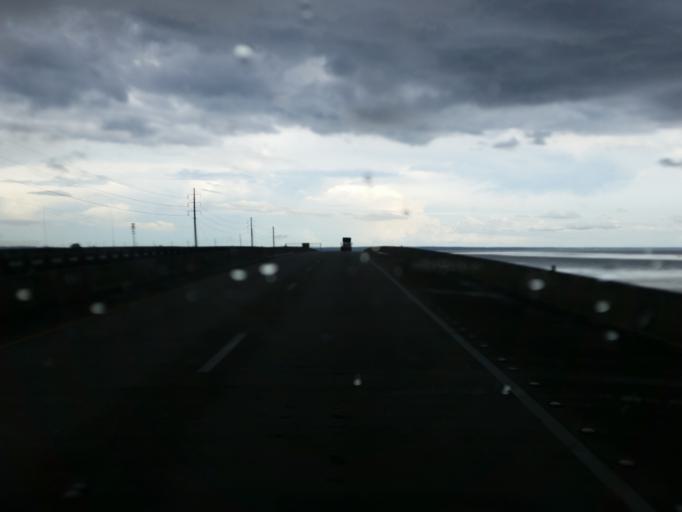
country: US
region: Alabama
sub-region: Mobile County
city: Mobile
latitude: 30.6844
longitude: -88.0100
